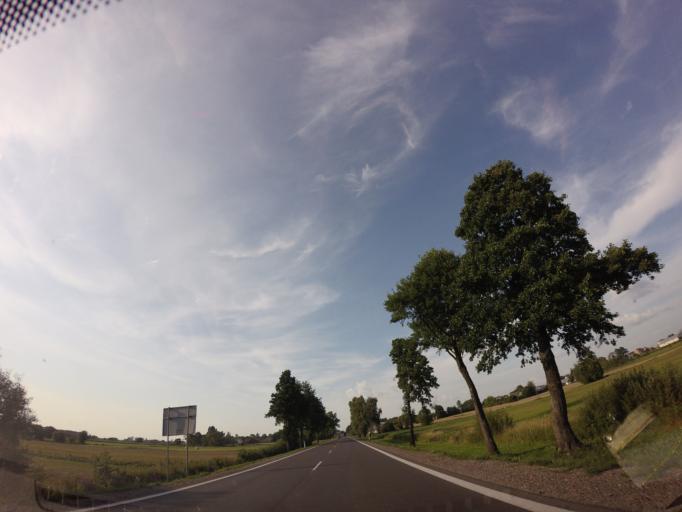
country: PL
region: Podlasie
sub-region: Powiat sokolski
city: Suchowola
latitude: 53.4587
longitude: 23.0884
